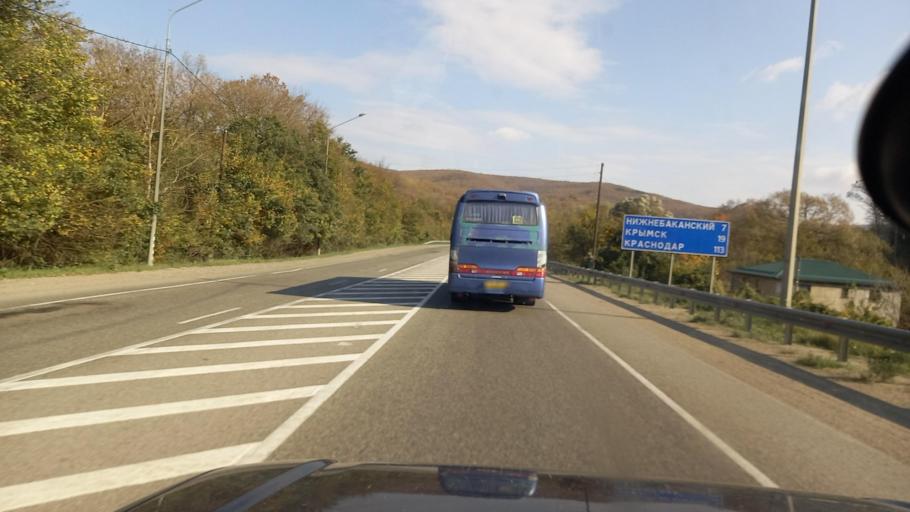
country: RU
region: Krasnodarskiy
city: Verkhnebakanskiy
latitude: 44.8712
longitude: 37.7563
